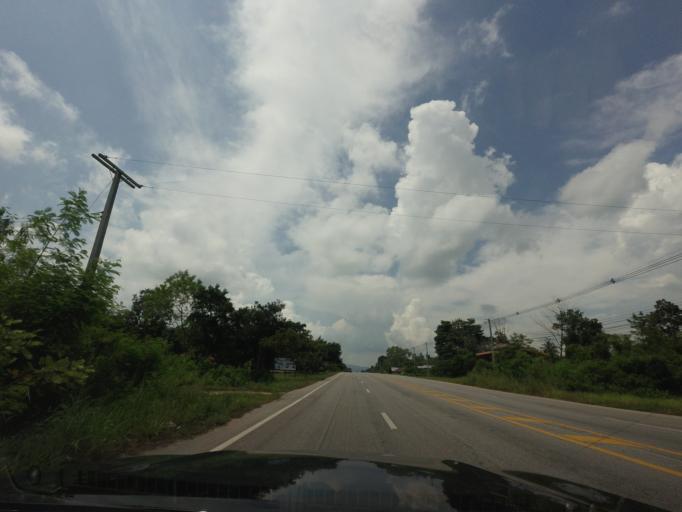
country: TH
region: Khon Kaen
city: Phu Wiang
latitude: 16.6790
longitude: 102.3426
